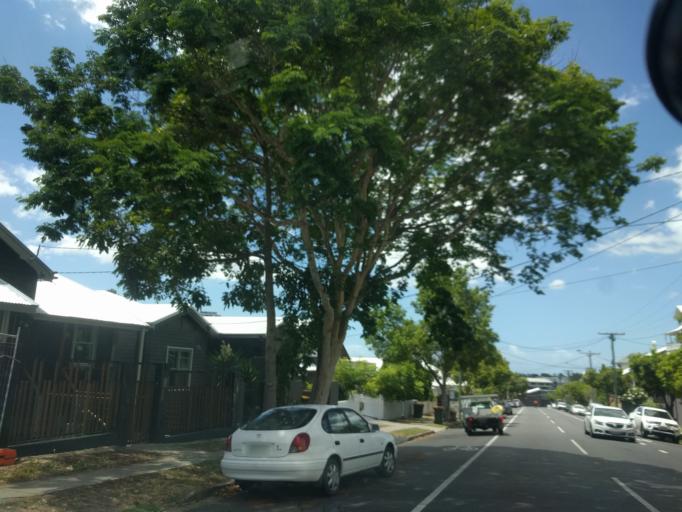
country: AU
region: Queensland
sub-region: Brisbane
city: Fortitude Valley
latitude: -27.4565
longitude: 153.0454
